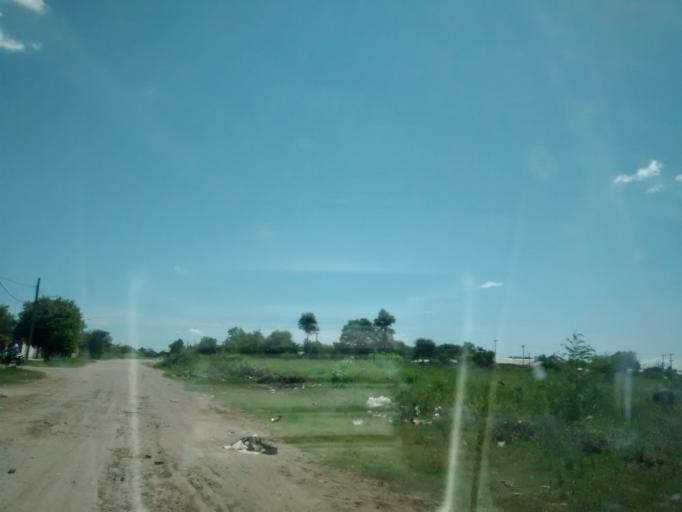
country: AR
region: Chaco
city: Fontana
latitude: -27.4002
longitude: -58.9890
